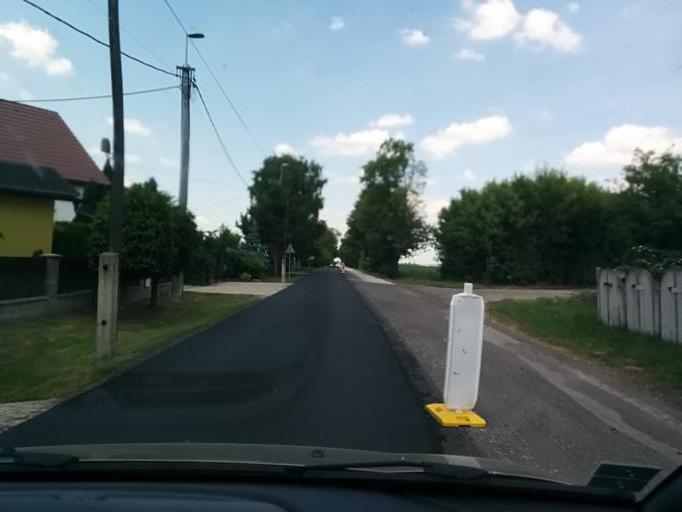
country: SK
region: Trnavsky
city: Sladkovicovo
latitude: 48.2358
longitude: 17.5718
